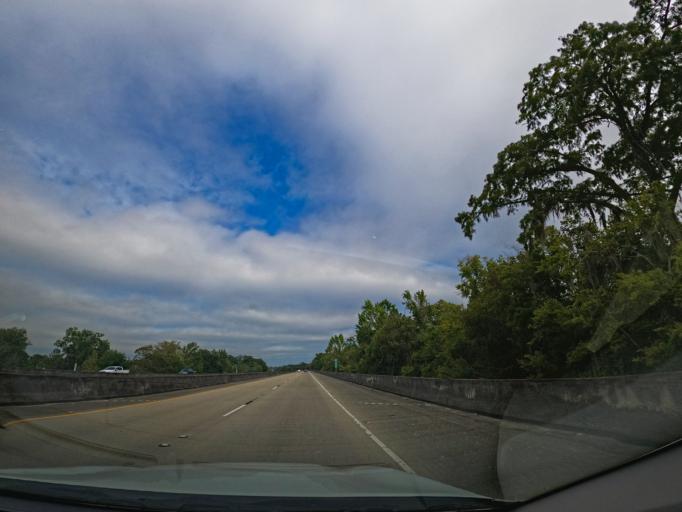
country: US
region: Louisiana
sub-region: Saint Mary Parish
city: Amelia
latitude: 29.6875
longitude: -91.1438
